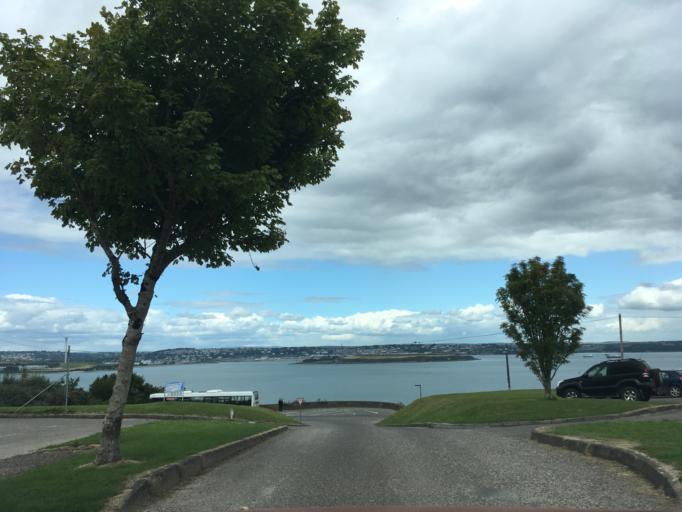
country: IE
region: Munster
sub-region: County Cork
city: Crosshaven
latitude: 51.8089
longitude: -8.2809
